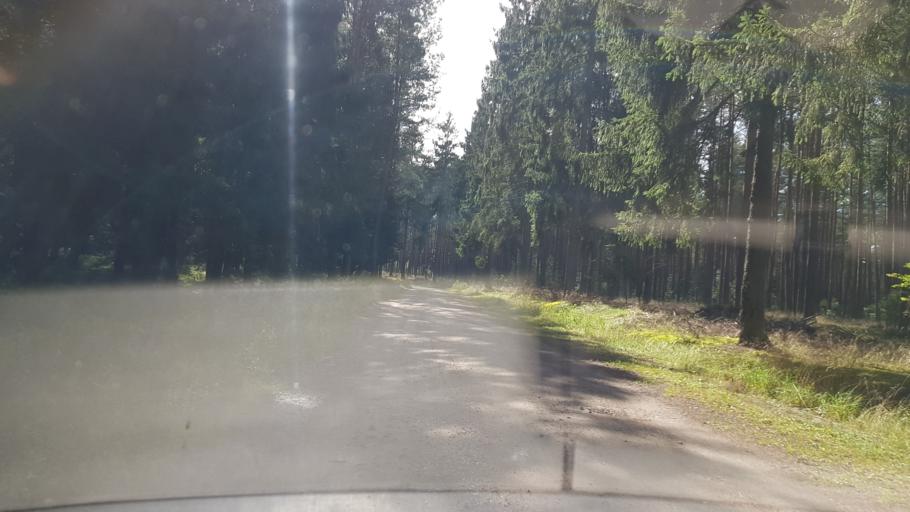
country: PL
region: West Pomeranian Voivodeship
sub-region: Powiat bialogardzki
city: Tychowo
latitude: 54.0220
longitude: 16.2989
